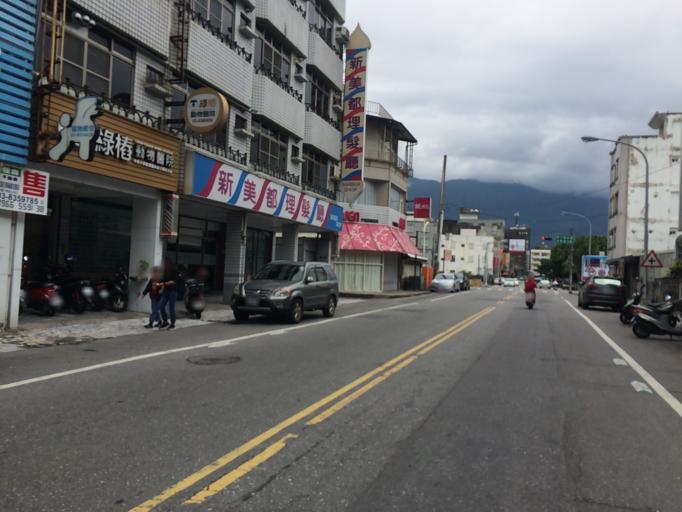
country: TW
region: Taiwan
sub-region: Hualien
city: Hualian
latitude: 23.9825
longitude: 121.6084
